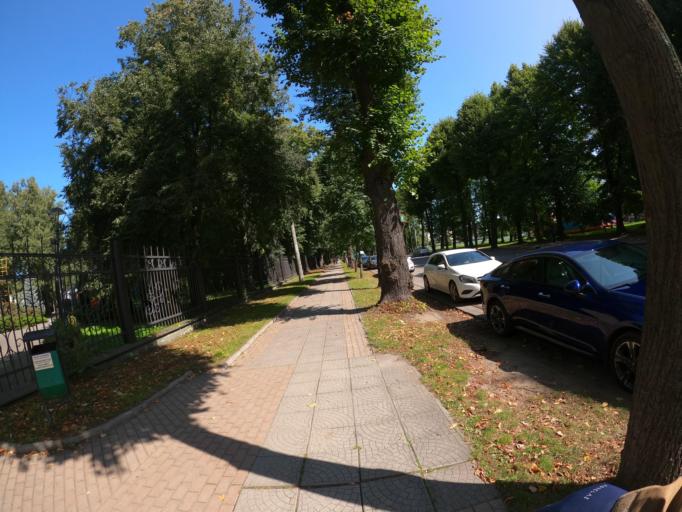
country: RU
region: Kaliningrad
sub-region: Gorod Kaliningrad
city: Kaliningrad
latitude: 54.7268
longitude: 20.5147
